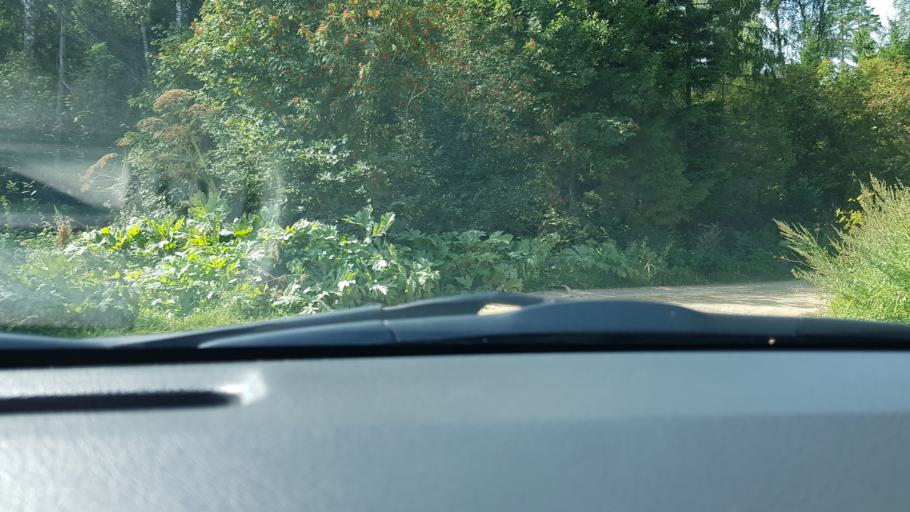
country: RU
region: Moskovskaya
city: Istra
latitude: 56.0009
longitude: 36.9147
